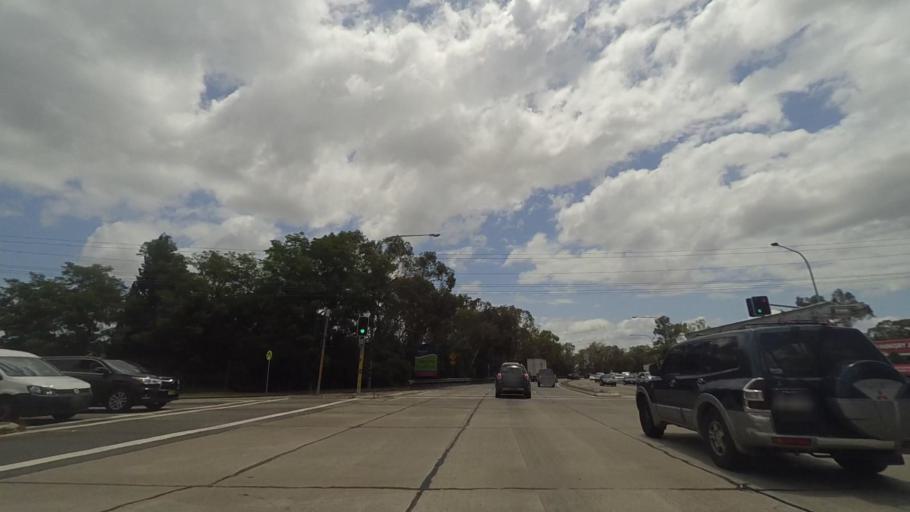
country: AU
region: New South Wales
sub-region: Fairfield
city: Cabramatta West
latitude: -33.8995
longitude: 150.9191
